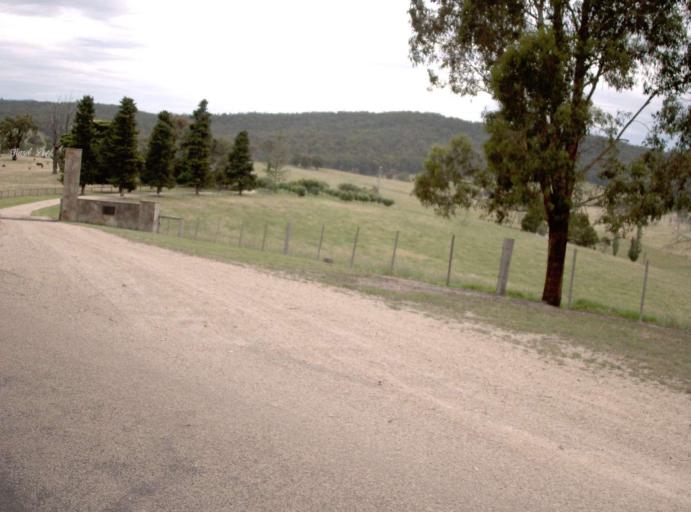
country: AU
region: Victoria
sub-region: East Gippsland
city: Bairnsdale
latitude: -37.7282
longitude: 147.5897
